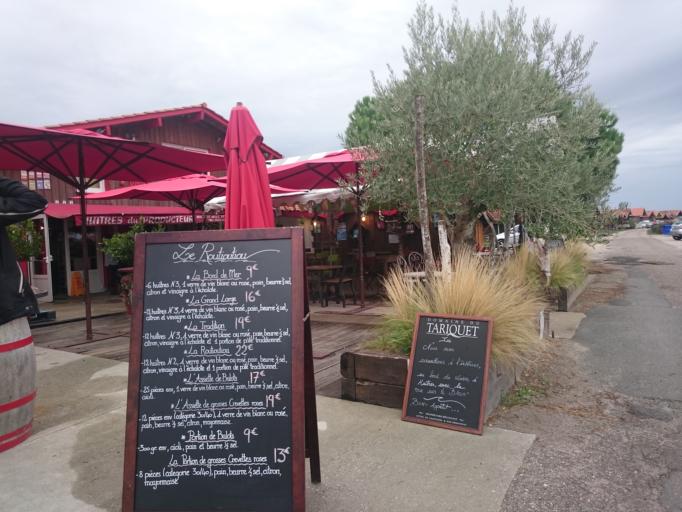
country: FR
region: Aquitaine
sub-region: Departement de la Gironde
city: Gujan-Mestras
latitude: 44.6427
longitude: -1.0733
